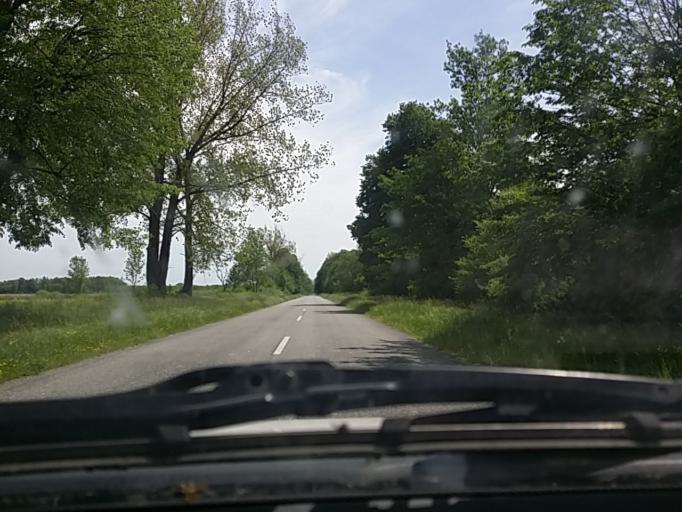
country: HU
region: Baranya
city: Sellye
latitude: 45.9200
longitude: 17.6651
